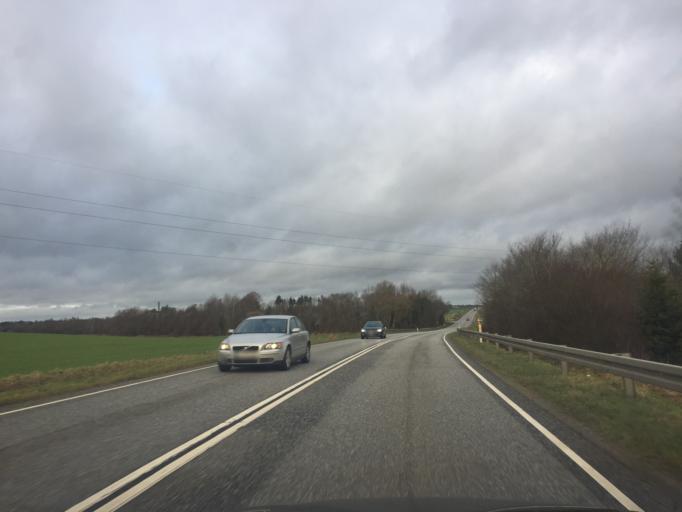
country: DK
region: Zealand
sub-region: Soro Kommune
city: Soro
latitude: 55.4754
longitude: 11.5672
